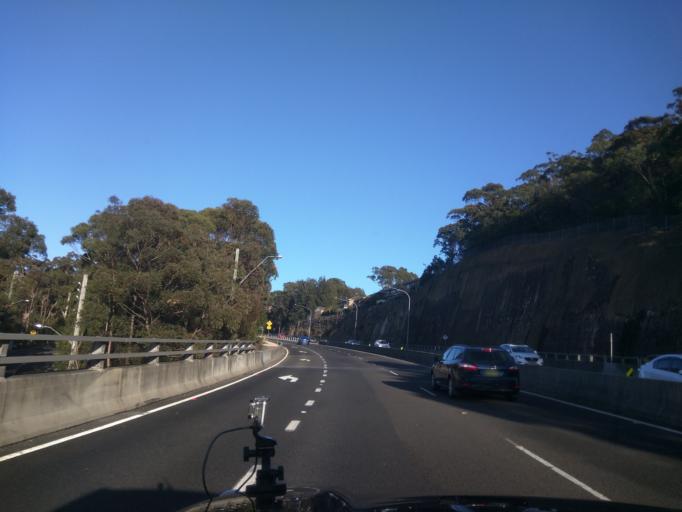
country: AU
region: New South Wales
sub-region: Sutherland Shire
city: Bonnet Bay
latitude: -34.0193
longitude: 151.0463
